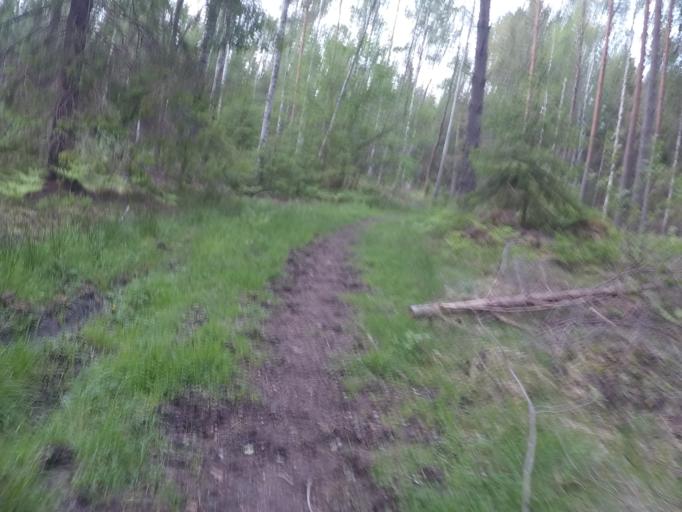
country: SE
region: Soedermanland
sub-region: Eskilstuna Kommun
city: Kvicksund
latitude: 59.4077
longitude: 16.3222
